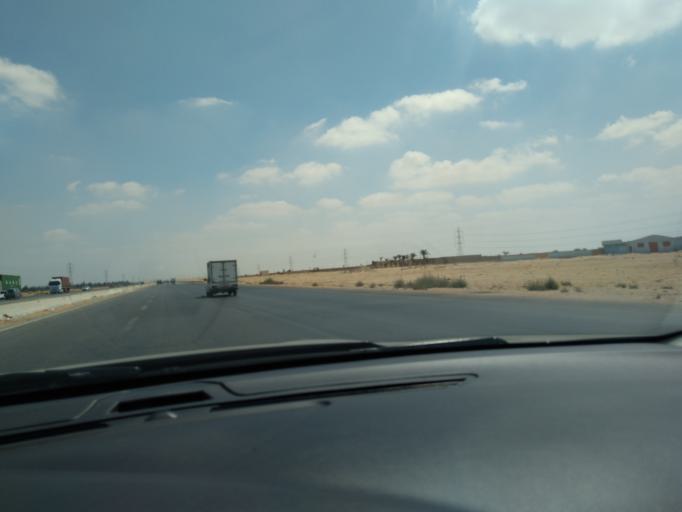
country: EG
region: Al Isma'iliyah
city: At Tall al Kabir
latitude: 30.3511
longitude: 31.8858
